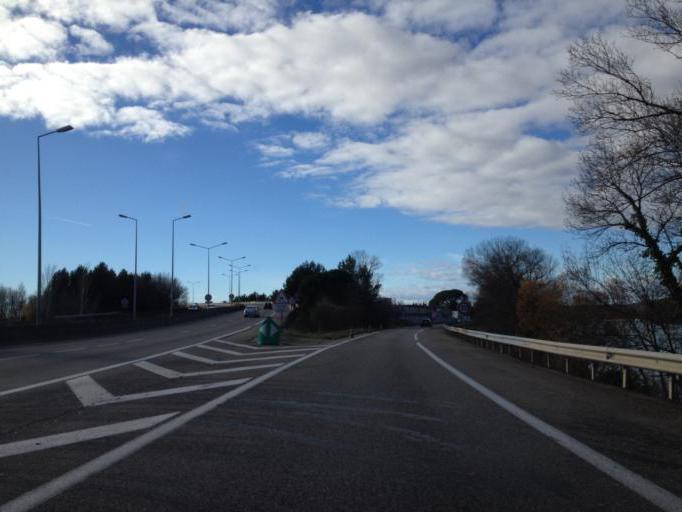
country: FR
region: Provence-Alpes-Cote d'Azur
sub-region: Departement du Vaucluse
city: Le Pontet
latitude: 43.9588
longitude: 4.8432
